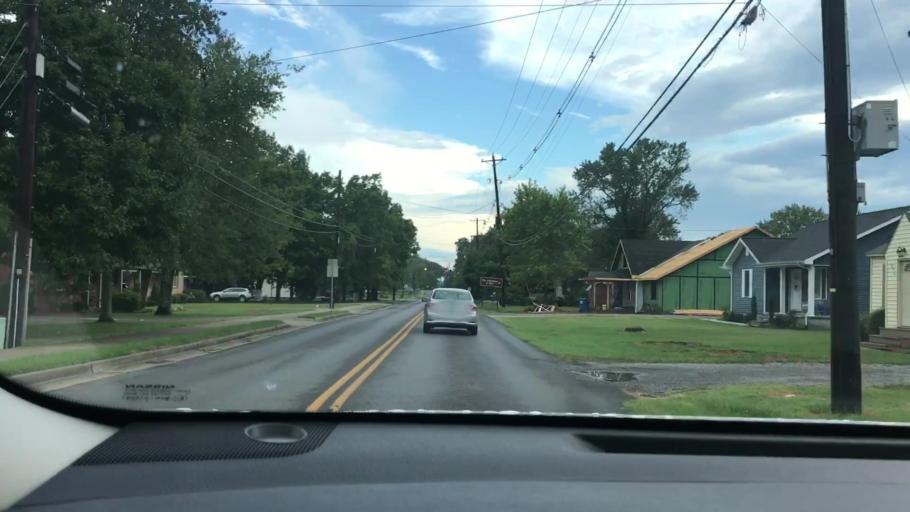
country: US
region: Kentucky
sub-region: Calloway County
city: Murray
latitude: 36.6080
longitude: -88.3245
